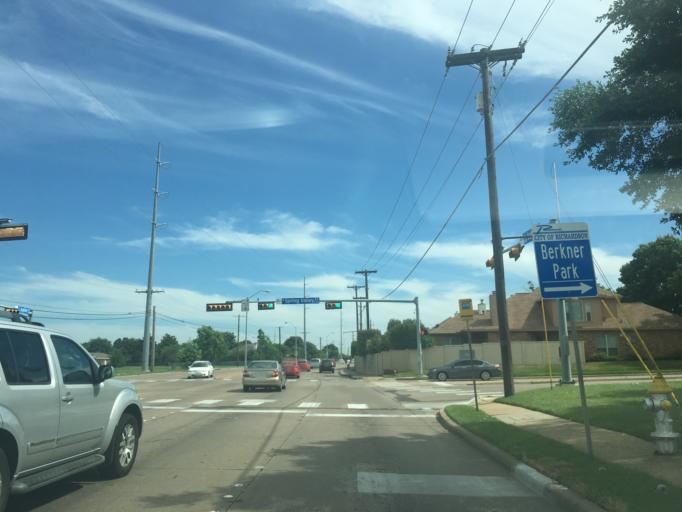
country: US
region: Texas
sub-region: Dallas County
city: Richardson
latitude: 32.9388
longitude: -96.6830
